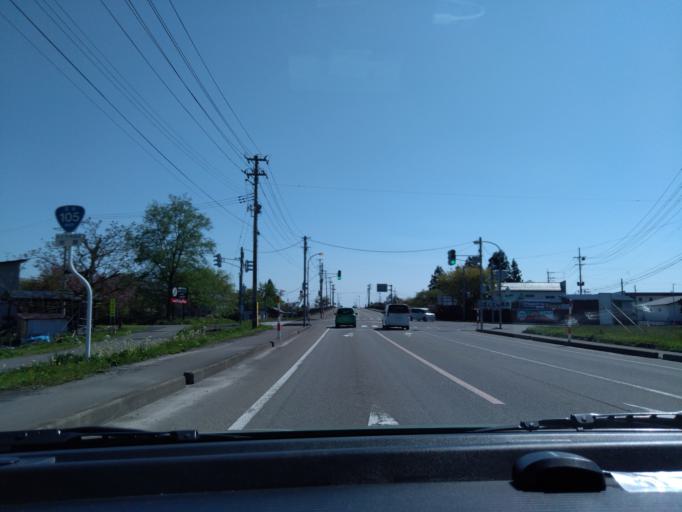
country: JP
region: Akita
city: Kakunodatemachi
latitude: 39.5833
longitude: 140.5696
